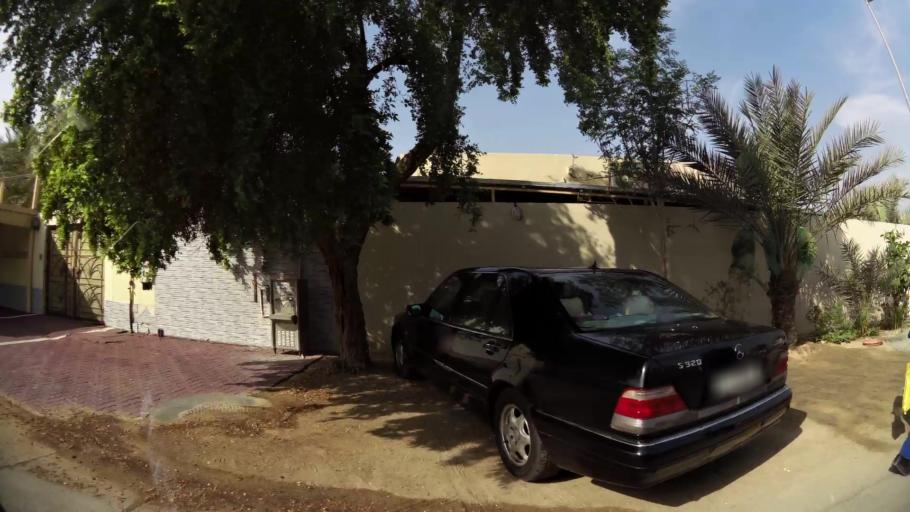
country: AE
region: Ash Shariqah
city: Sharjah
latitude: 25.2171
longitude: 55.3964
